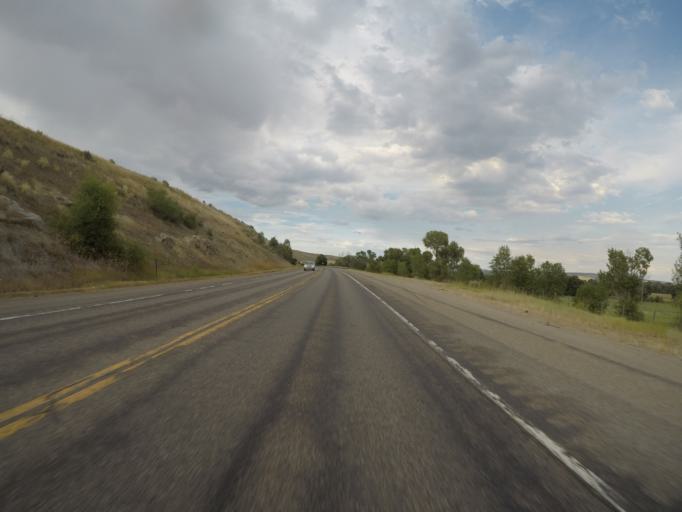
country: US
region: Colorado
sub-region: Moffat County
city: Craig
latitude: 40.5258
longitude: -107.4617
